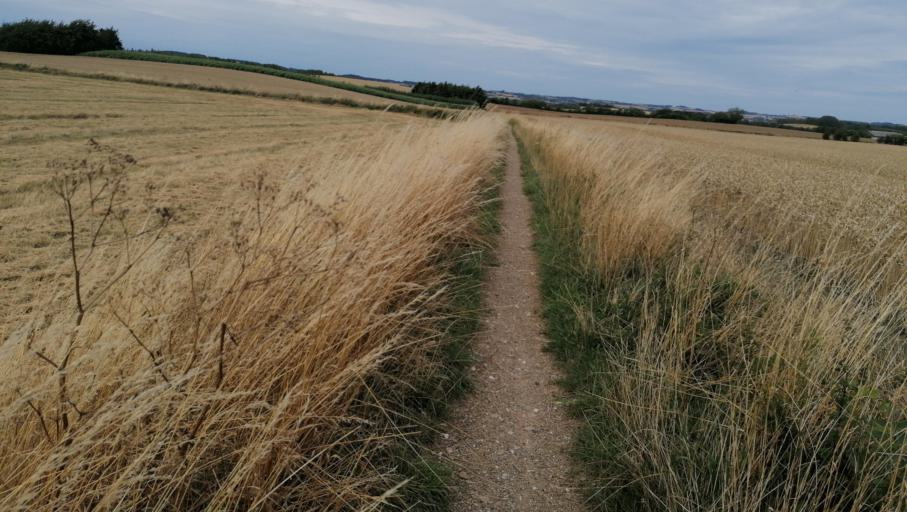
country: DK
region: Zealand
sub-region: Odsherred Kommune
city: Horve
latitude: 55.7506
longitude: 11.4293
